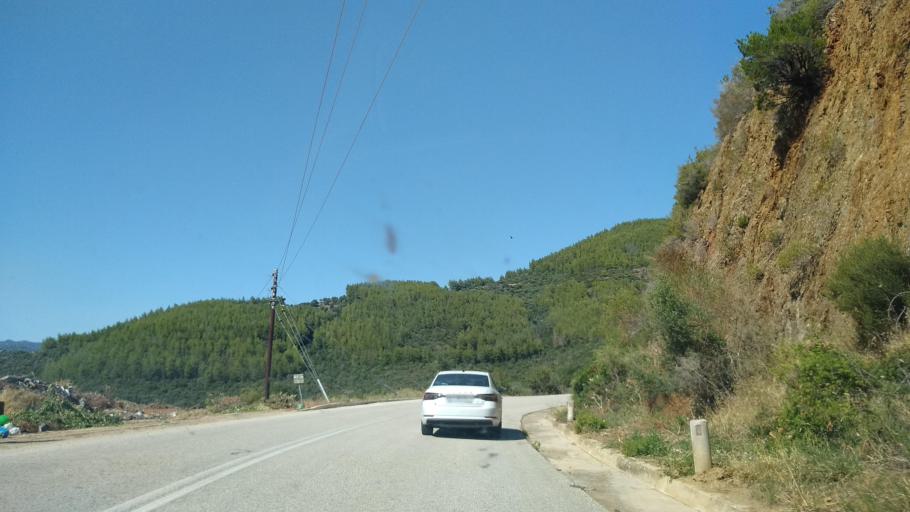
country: GR
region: Central Macedonia
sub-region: Nomos Chalkidikis
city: Sykia
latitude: 39.9771
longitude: 23.9112
